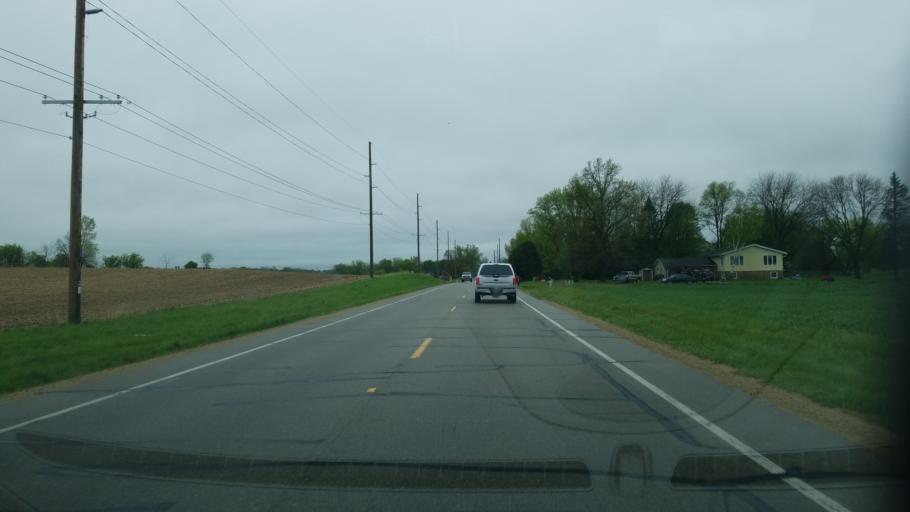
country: US
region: Wisconsin
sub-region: Dane County
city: Fitchburg
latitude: 42.9341
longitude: -89.4378
